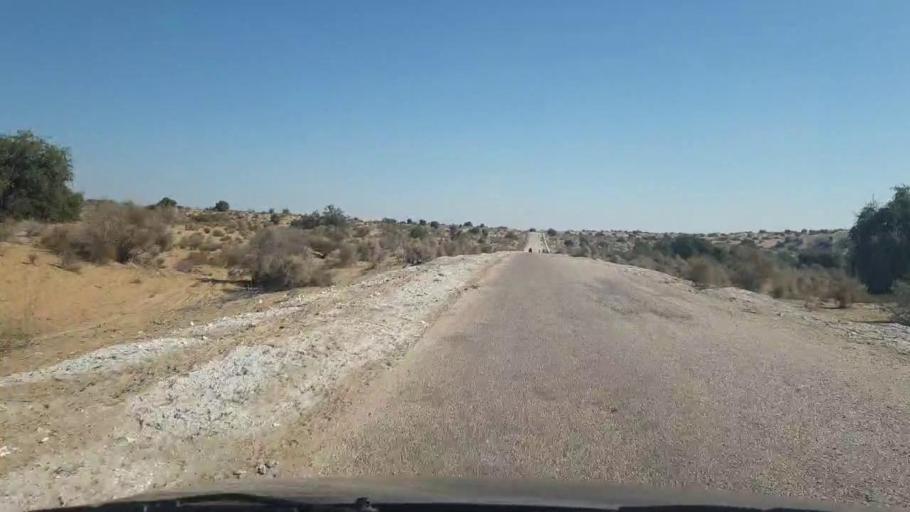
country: PK
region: Sindh
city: Bozdar
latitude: 27.0048
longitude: 68.8779
